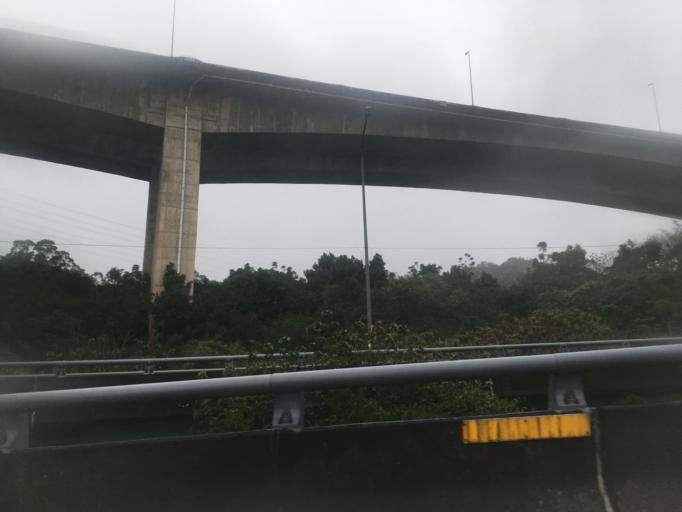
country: TW
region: Taiwan
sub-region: Keelung
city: Keelung
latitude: 25.1146
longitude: 121.6906
